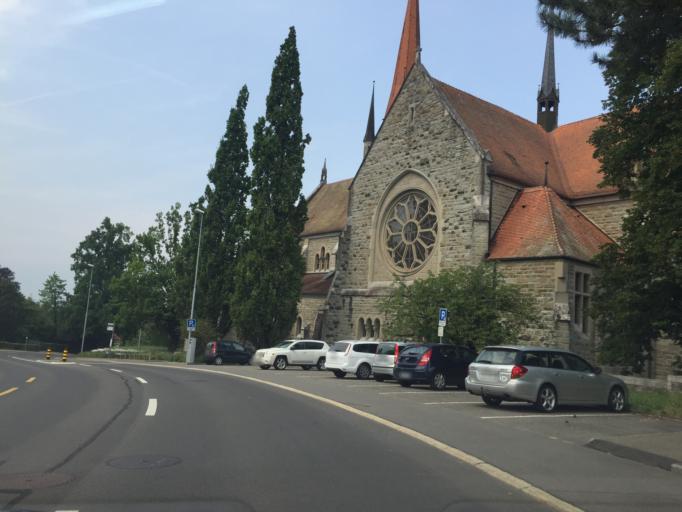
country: CH
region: Zug
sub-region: Zug
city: Zug
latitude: 47.1622
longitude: 8.5179
